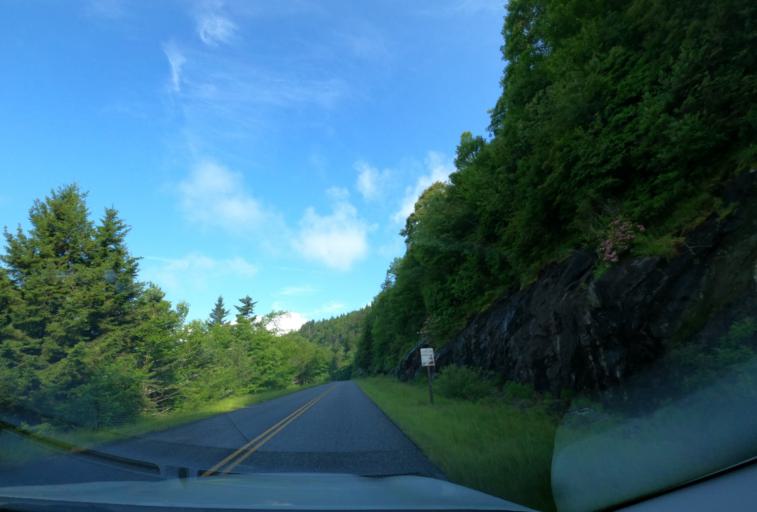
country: US
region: North Carolina
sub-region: Haywood County
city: Hazelwood
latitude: 35.3014
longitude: -82.9333
